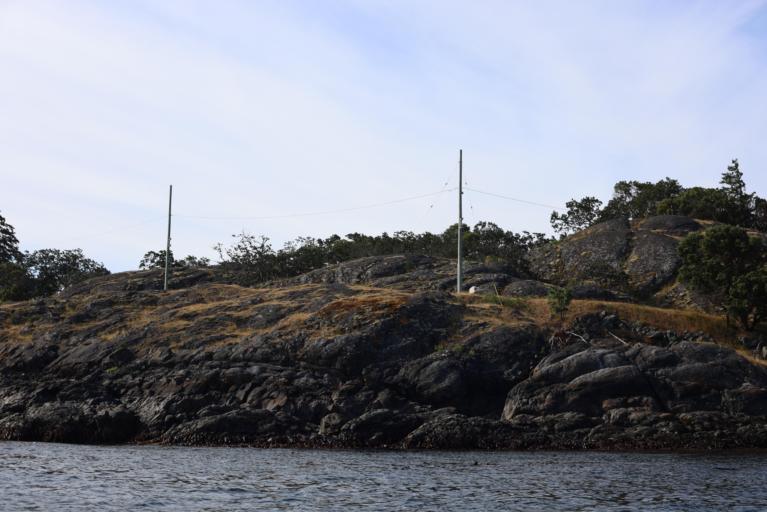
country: CA
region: British Columbia
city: Metchosin
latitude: 48.3429
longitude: -123.5308
